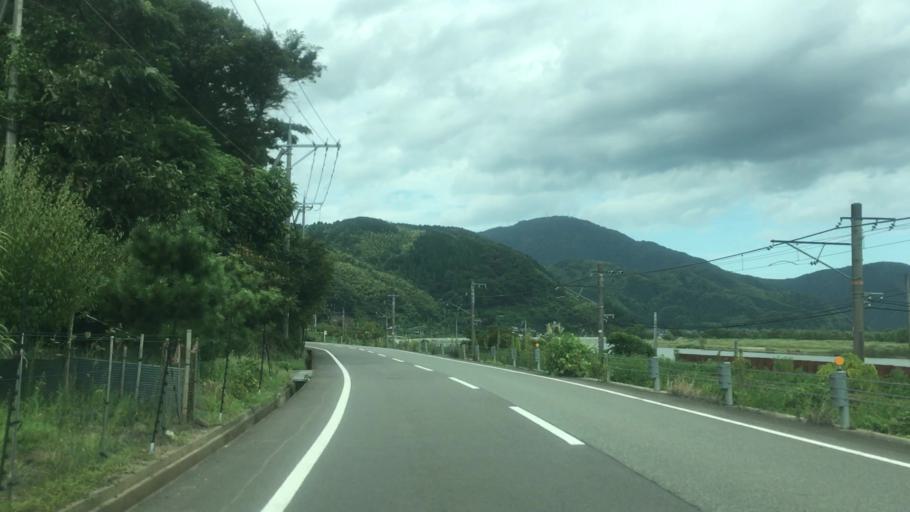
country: JP
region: Hyogo
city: Toyooka
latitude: 35.5752
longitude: 134.8044
